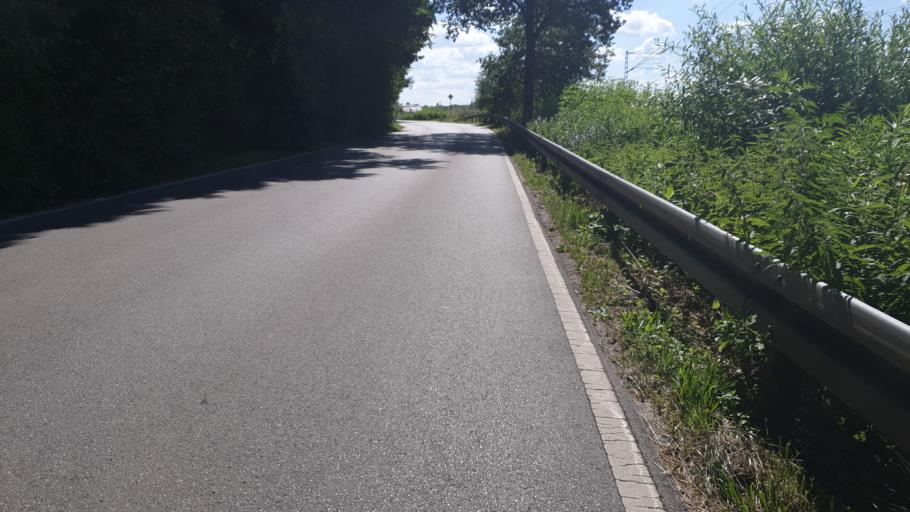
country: DE
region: Bavaria
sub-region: Upper Bavaria
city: Germering
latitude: 48.1609
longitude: 11.3926
